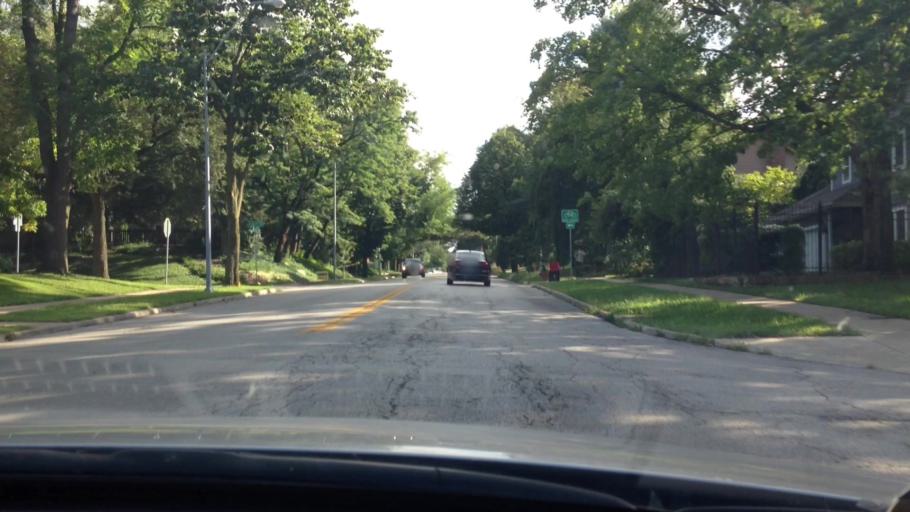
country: US
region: Kansas
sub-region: Johnson County
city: Mission Hills
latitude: 39.0181
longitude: -94.5930
